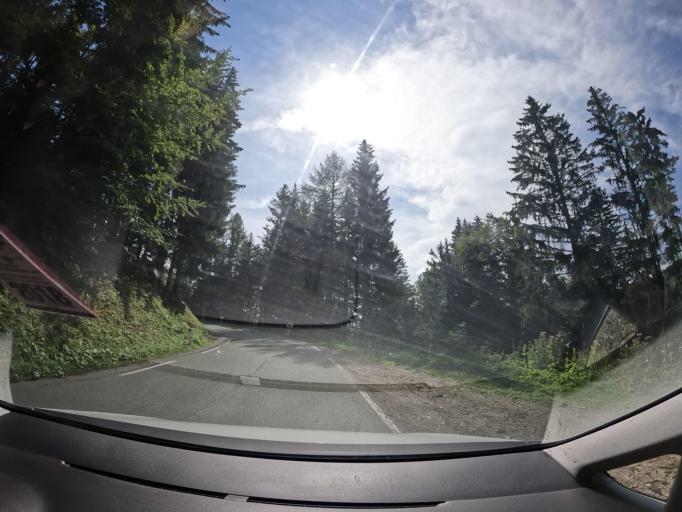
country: AT
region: Carinthia
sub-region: Politischer Bezirk Feldkirchen
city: Glanegg
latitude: 46.7509
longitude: 14.2221
